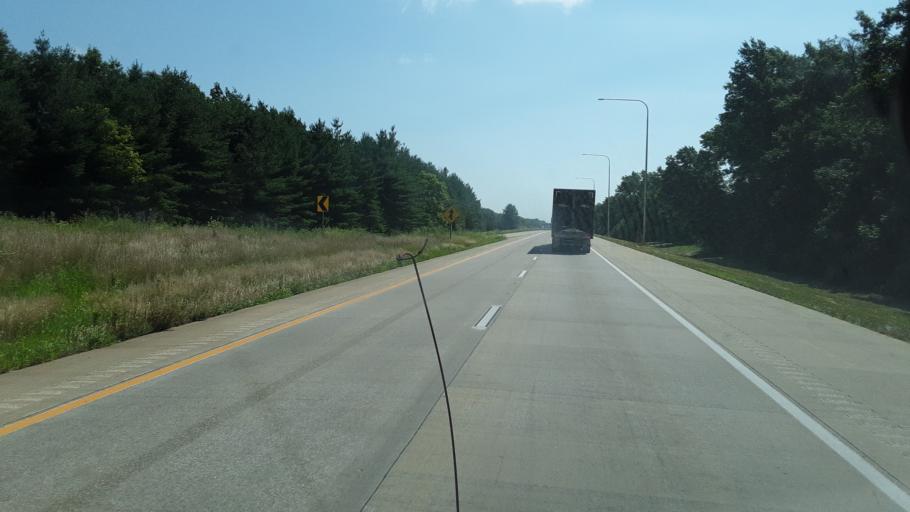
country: US
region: Illinois
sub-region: Effingham County
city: Teutopolis
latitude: 39.1493
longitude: -88.5061
